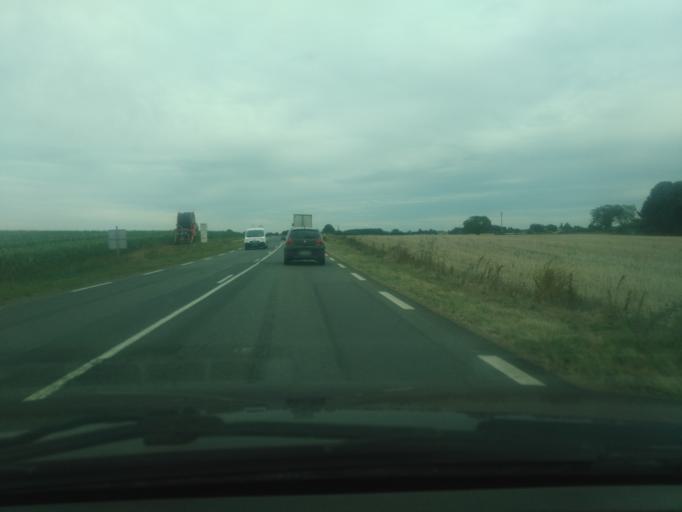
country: FR
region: Poitou-Charentes
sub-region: Departement de la Vienne
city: Saint-Savin
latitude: 46.5690
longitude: 0.8415
